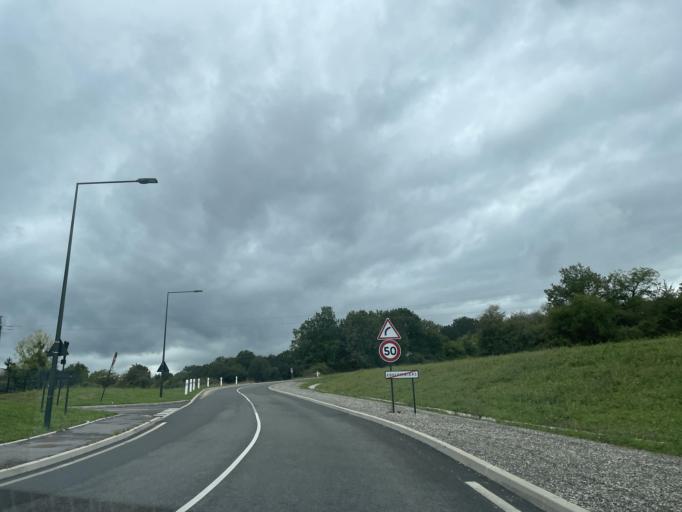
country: FR
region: Ile-de-France
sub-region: Departement de Seine-et-Marne
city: Coulommiers
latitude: 48.8158
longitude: 3.1072
